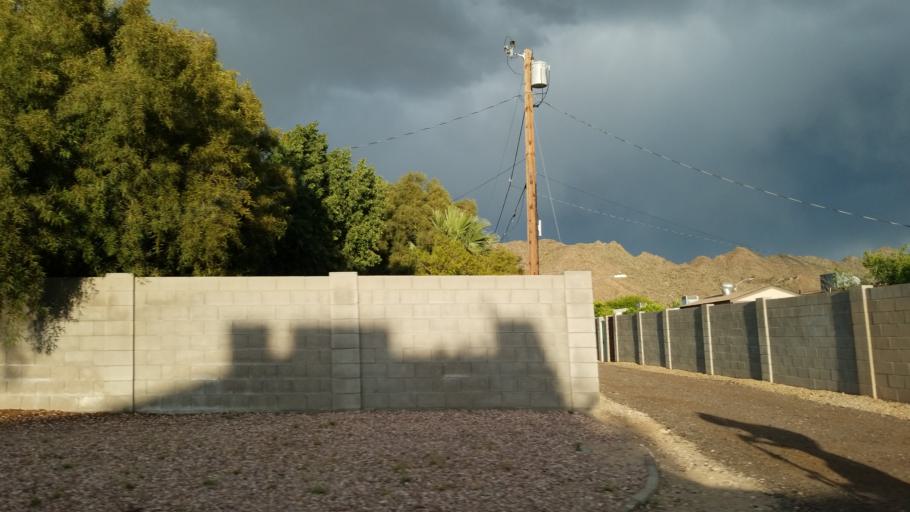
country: US
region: Arizona
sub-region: Maricopa County
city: Paradise Valley
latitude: 33.5834
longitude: -112.0565
